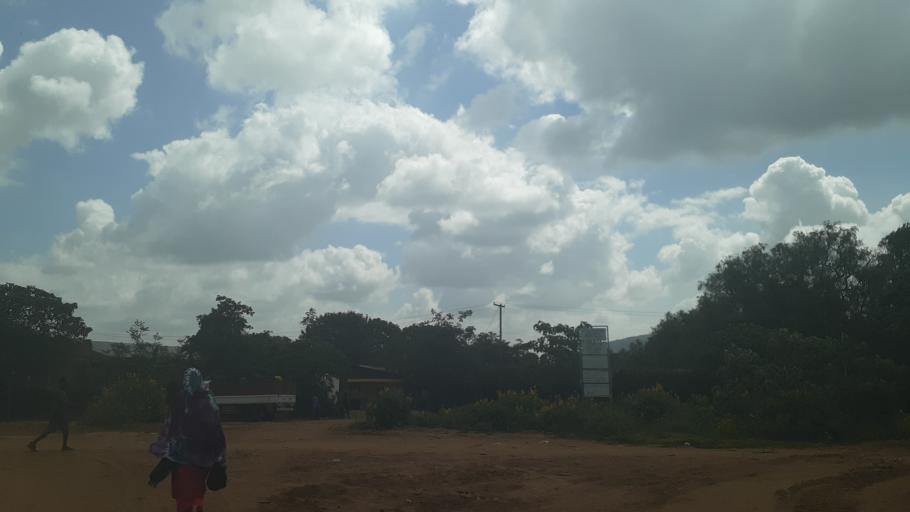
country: ET
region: Oromiya
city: Yabelo
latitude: 4.8952
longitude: 38.0979
